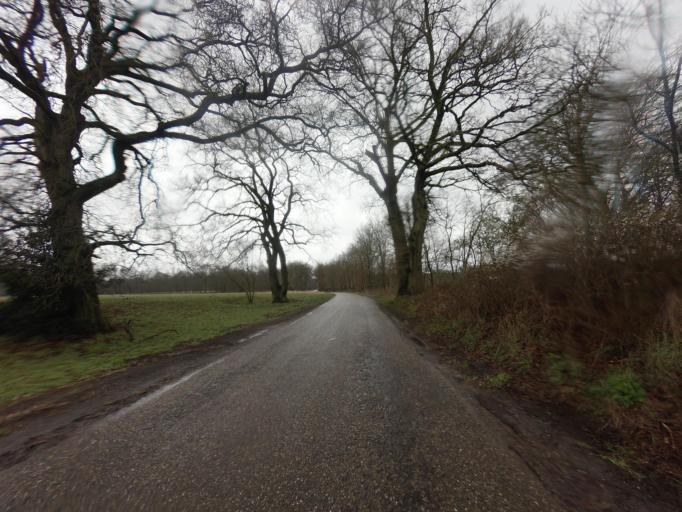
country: NL
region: Gelderland
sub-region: Gemeente Epe
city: Vaassen
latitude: 52.3120
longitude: 5.8953
